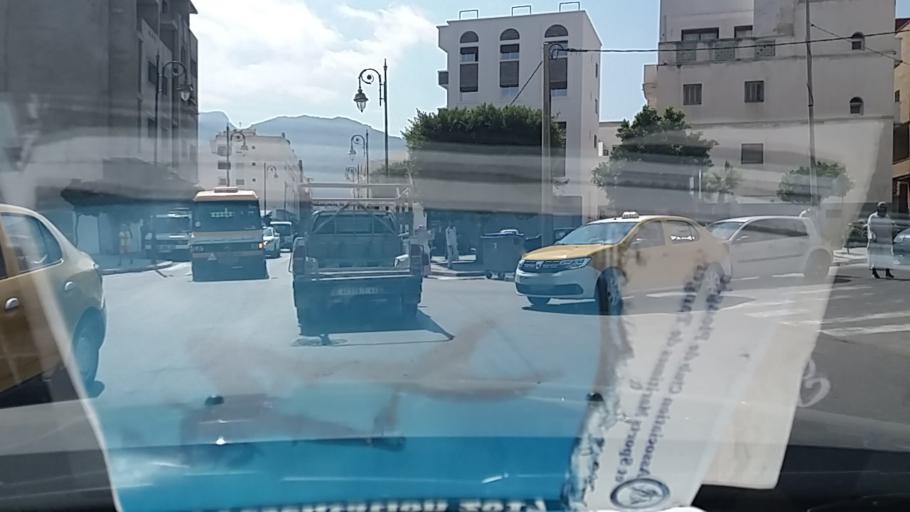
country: MA
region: Tanger-Tetouan
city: Tetouan
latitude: 35.5683
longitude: -5.3562
